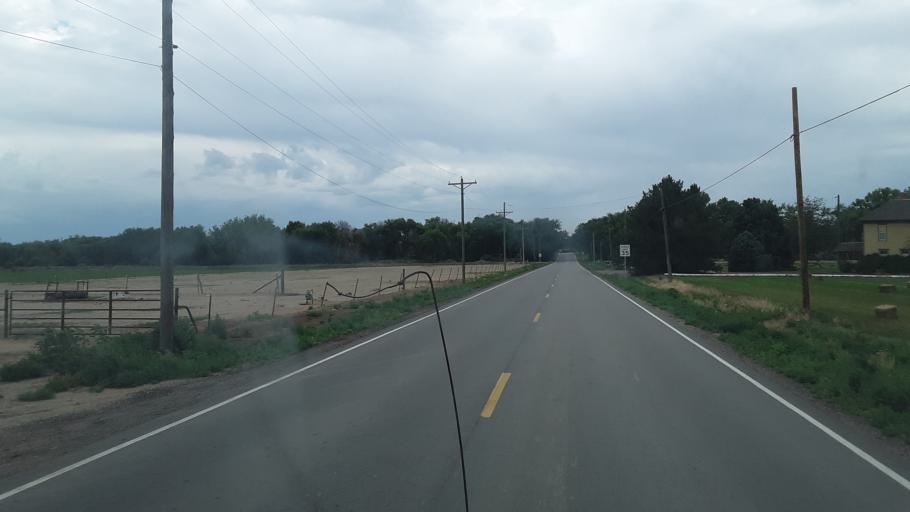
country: US
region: Colorado
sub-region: Otero County
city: Fowler
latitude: 38.1371
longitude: -104.0225
